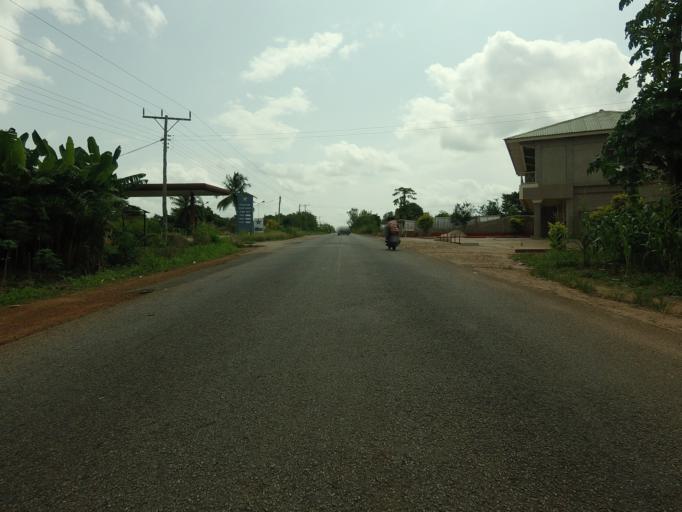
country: TG
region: Maritime
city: Lome
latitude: 6.2257
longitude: 1.0238
